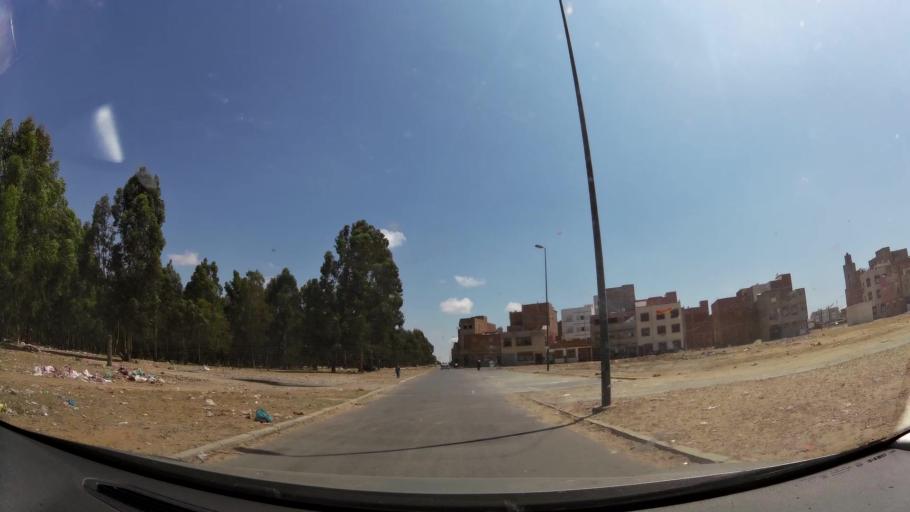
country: MA
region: Gharb-Chrarda-Beni Hssen
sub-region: Kenitra Province
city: Kenitra
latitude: 34.2432
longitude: -6.5366
